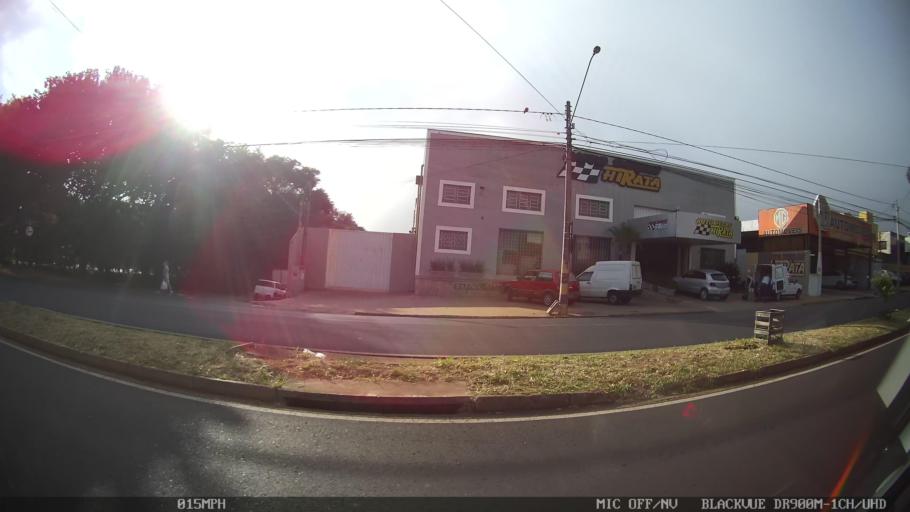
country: BR
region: Sao Paulo
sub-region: Sao Jose Do Rio Preto
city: Sao Jose do Rio Preto
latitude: -20.8380
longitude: -49.3711
